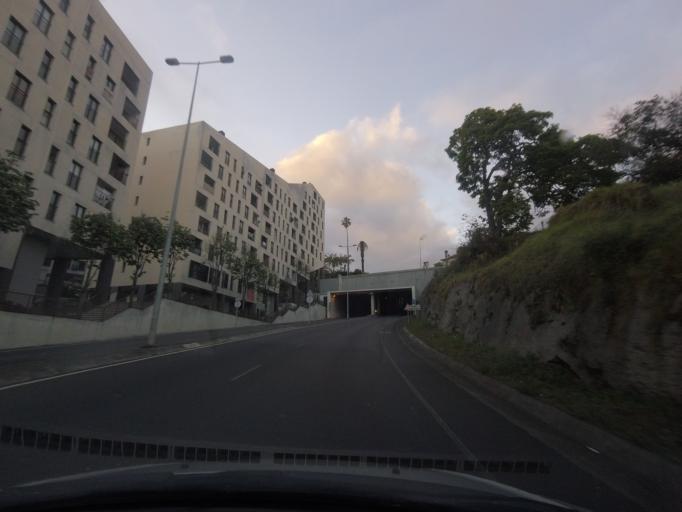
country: PT
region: Madeira
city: Camara de Lobos
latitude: 32.6485
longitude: -16.9400
